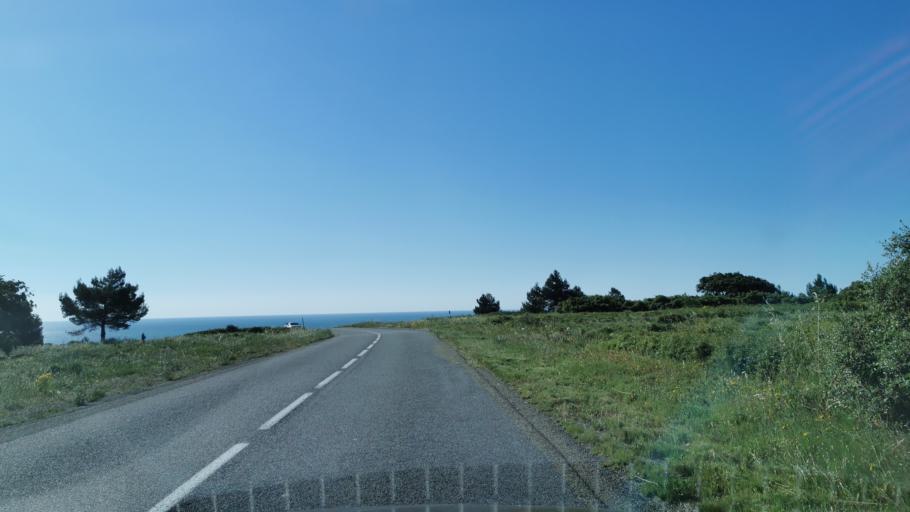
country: FR
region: Languedoc-Roussillon
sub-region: Departement de l'Aude
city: Armissan
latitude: 43.1622
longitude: 3.1357
